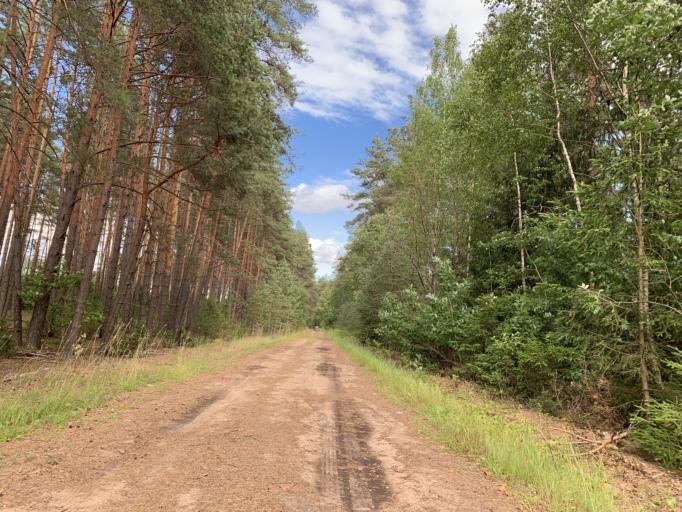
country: BY
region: Minsk
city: Ivyanyets
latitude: 53.9715
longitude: 26.8011
